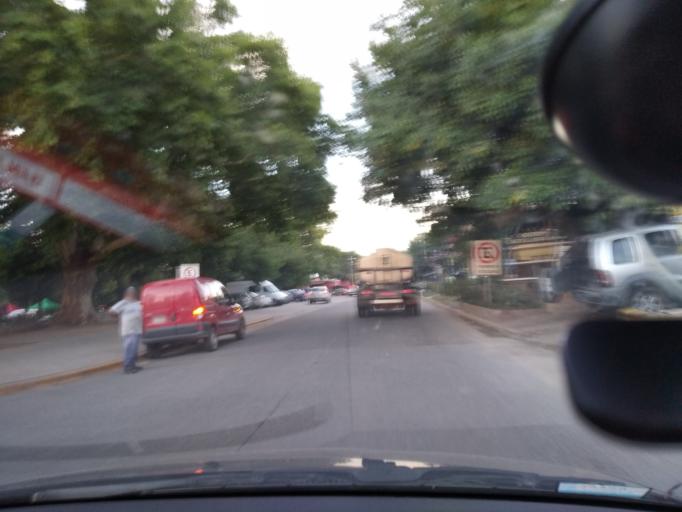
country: AR
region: Cordoba
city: Villa Las Rosas
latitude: -31.9478
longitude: -65.0517
